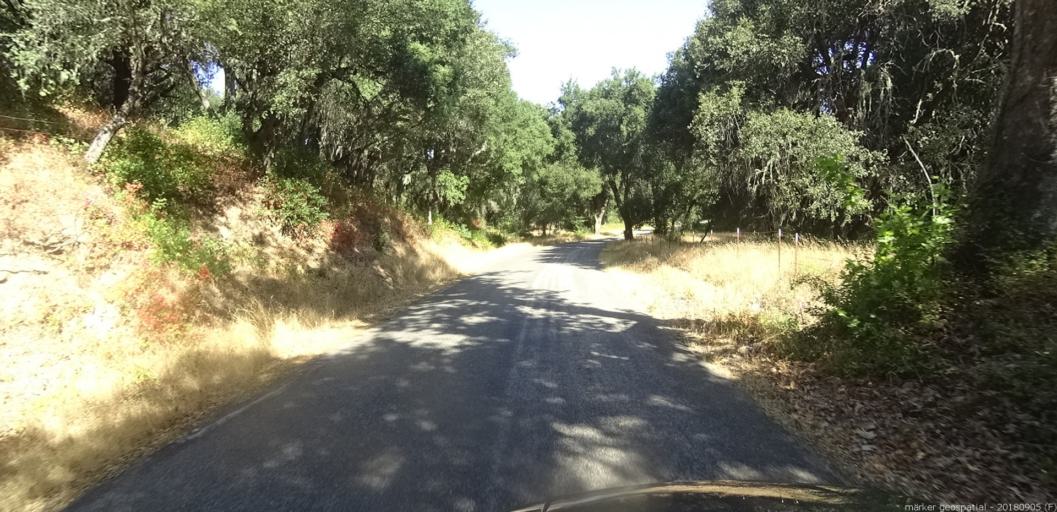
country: US
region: California
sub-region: Monterey County
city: Gonzales
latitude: 36.3465
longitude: -121.5426
